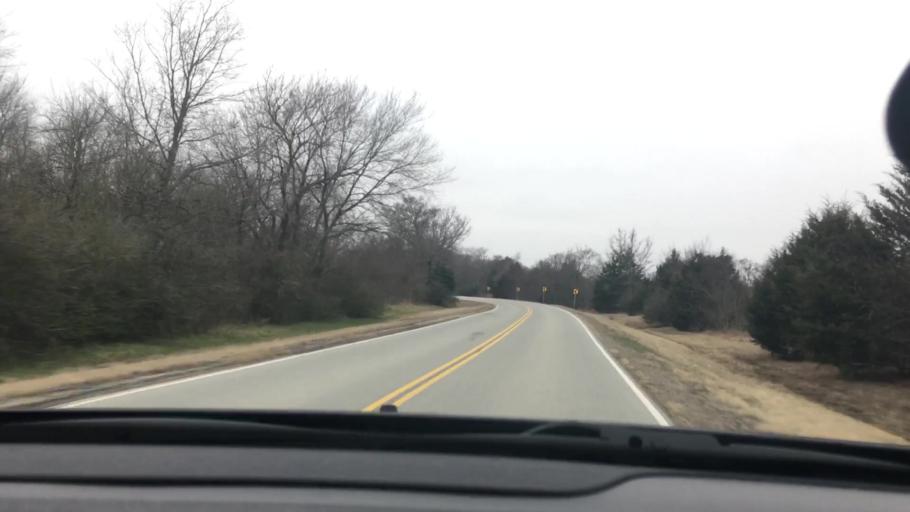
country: US
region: Oklahoma
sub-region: Coal County
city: Coalgate
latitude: 34.5309
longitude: -96.2604
